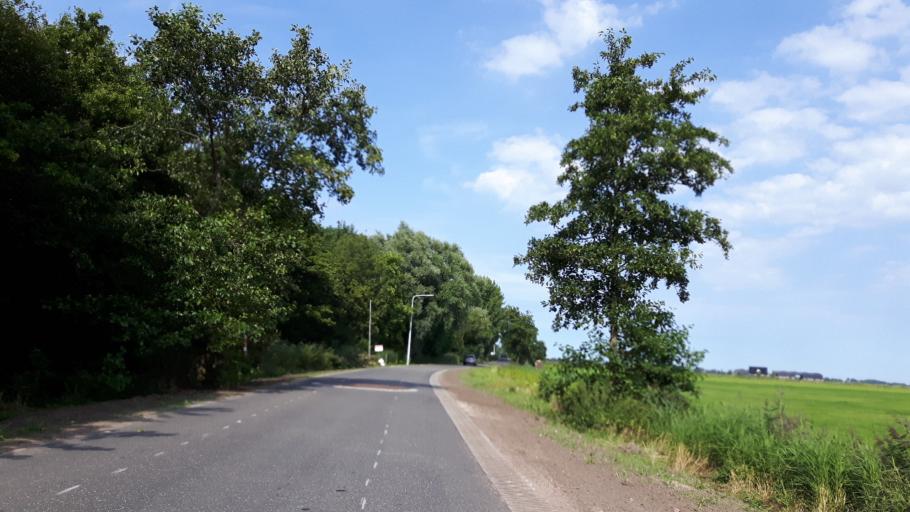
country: NL
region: Friesland
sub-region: Gemeente Ferwerderadiel
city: Burdaard
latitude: 53.2725
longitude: 5.8385
